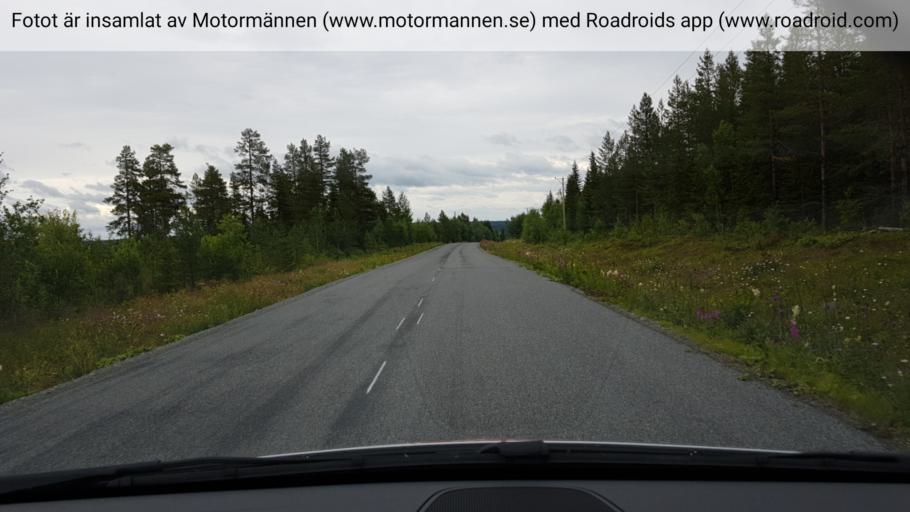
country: SE
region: Jaemtland
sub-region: Krokoms Kommun
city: Krokom
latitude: 63.6673
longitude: 14.5280
